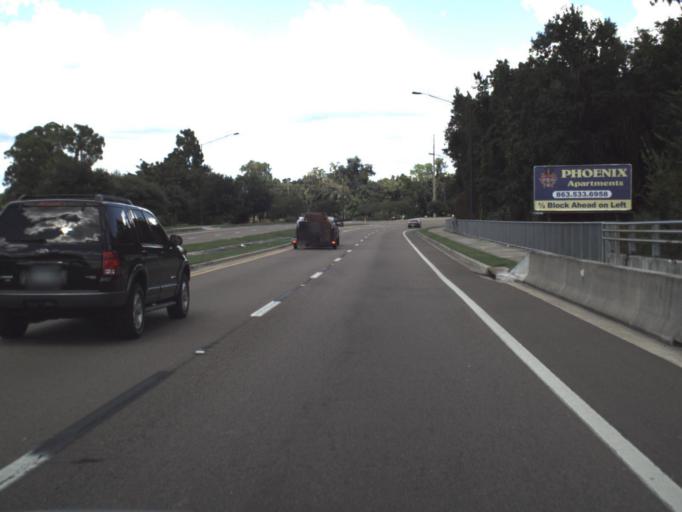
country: US
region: Florida
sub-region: Polk County
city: Bartow
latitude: 27.9020
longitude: -81.8487
